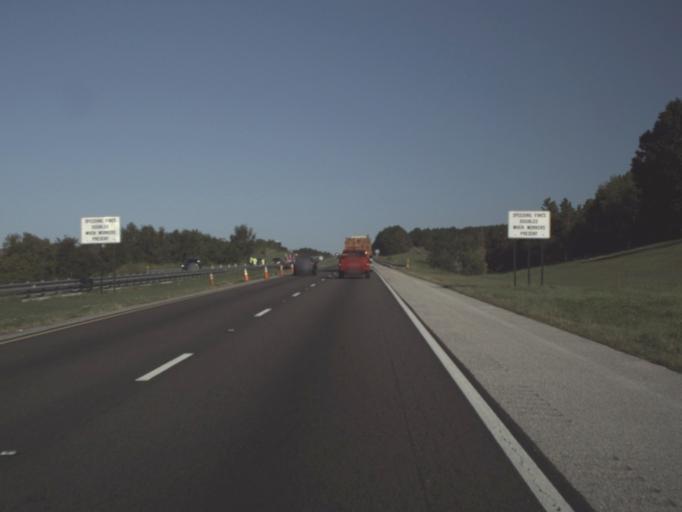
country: US
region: Florida
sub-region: Lake County
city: Montverde
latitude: 28.5777
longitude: -81.7014
